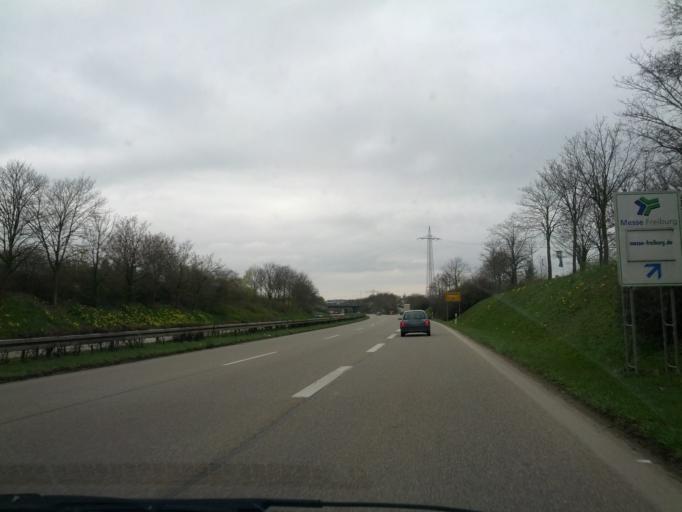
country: DE
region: Baden-Wuerttemberg
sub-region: Freiburg Region
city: Merzhausen
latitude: 47.9853
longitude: 7.8028
